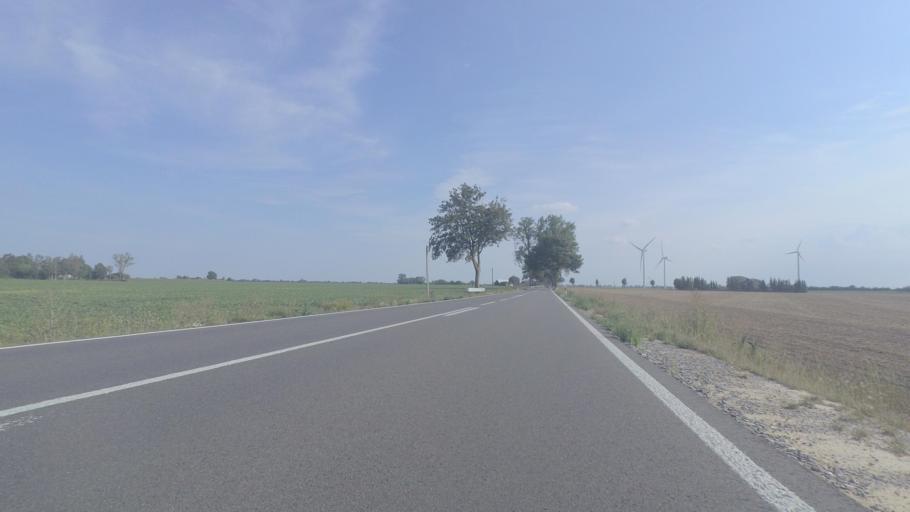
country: DE
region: Mecklenburg-Vorpommern
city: Grimmen
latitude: 54.0190
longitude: 13.1379
